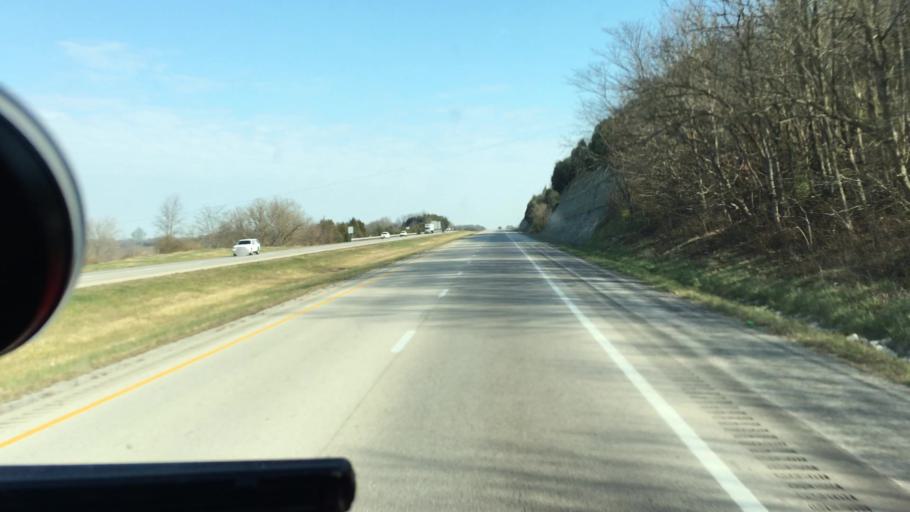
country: US
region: Kentucky
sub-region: Bath County
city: Owingsville
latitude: 38.1330
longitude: -83.7375
